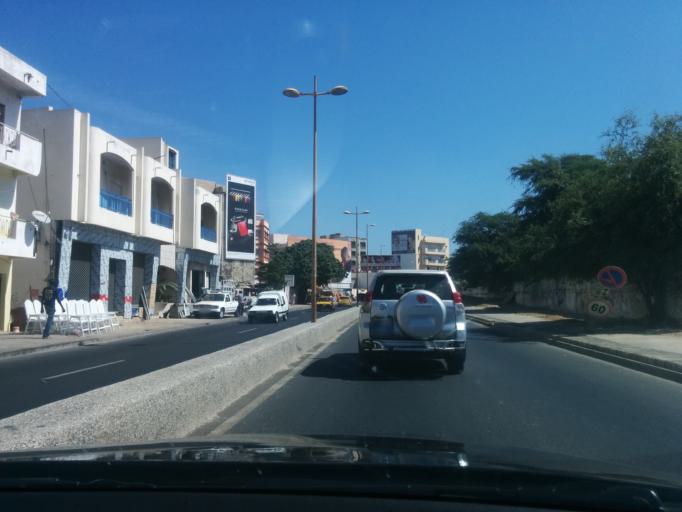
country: SN
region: Dakar
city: Dakar
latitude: 14.6764
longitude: -17.4555
